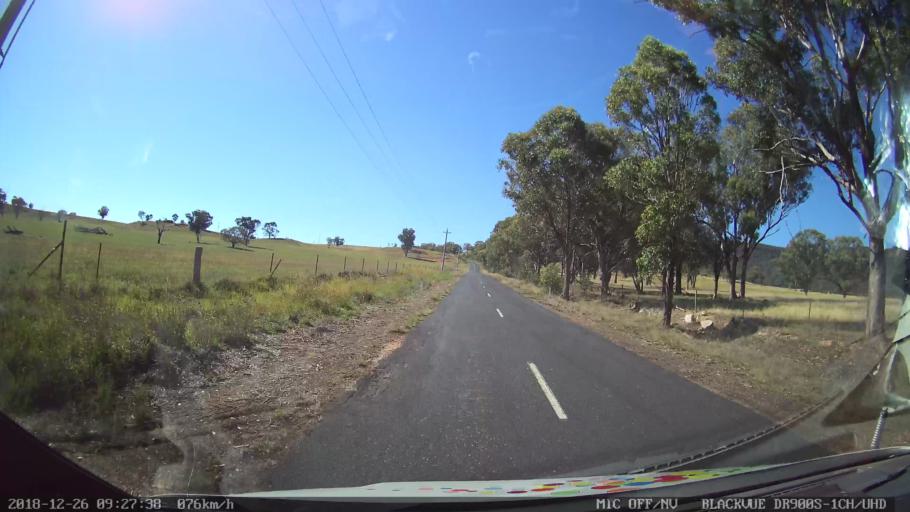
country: AU
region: New South Wales
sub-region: Mid-Western Regional
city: Kandos
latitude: -32.8378
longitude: 150.0180
